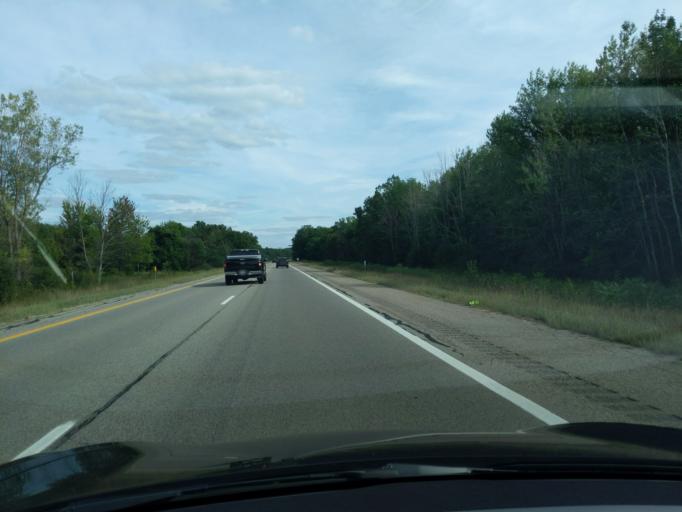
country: US
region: Michigan
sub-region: Muskegon County
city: Fruitport
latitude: 43.0965
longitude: -86.1042
